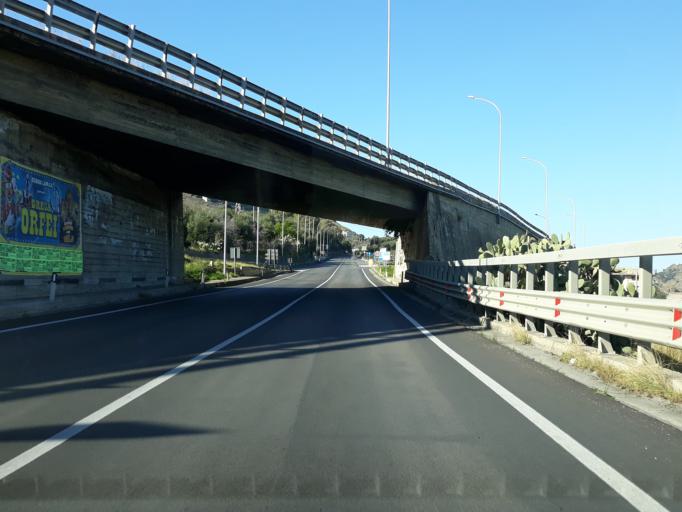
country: IT
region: Sicily
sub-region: Palermo
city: Misilmeri
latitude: 38.0431
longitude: 13.4607
